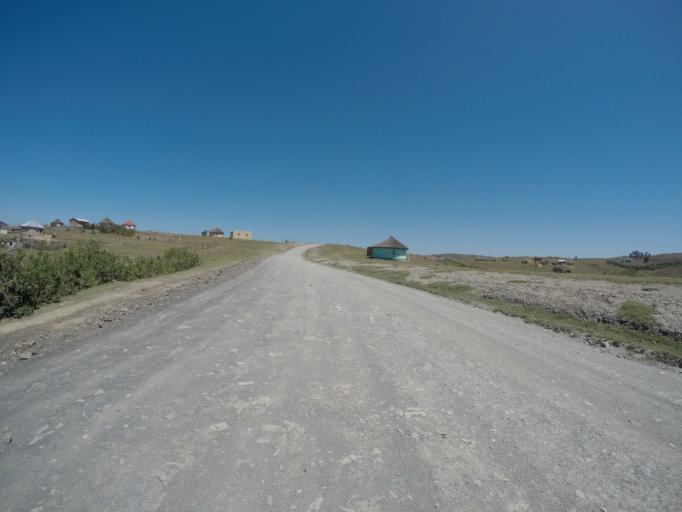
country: ZA
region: Eastern Cape
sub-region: OR Tambo District Municipality
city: Libode
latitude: -31.9941
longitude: 29.0574
